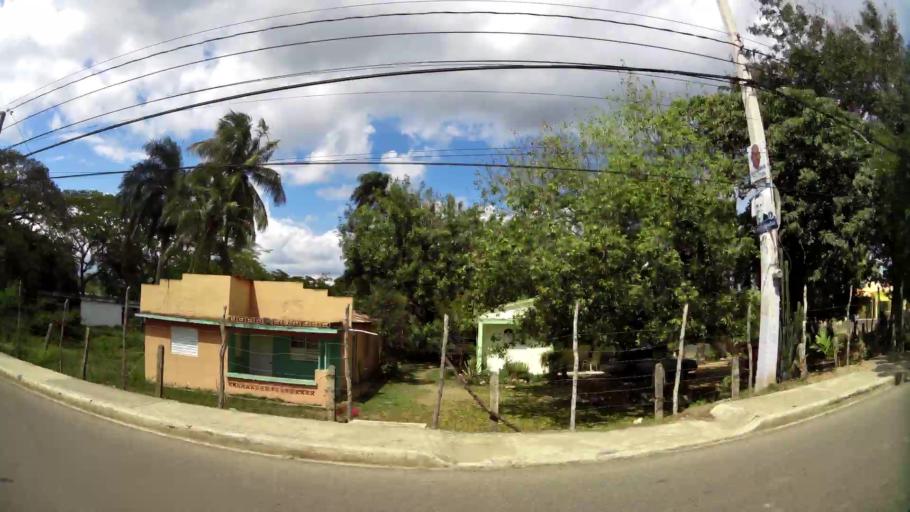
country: DO
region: Santiago
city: Santiago de los Caballeros
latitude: 19.4041
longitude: -70.6601
